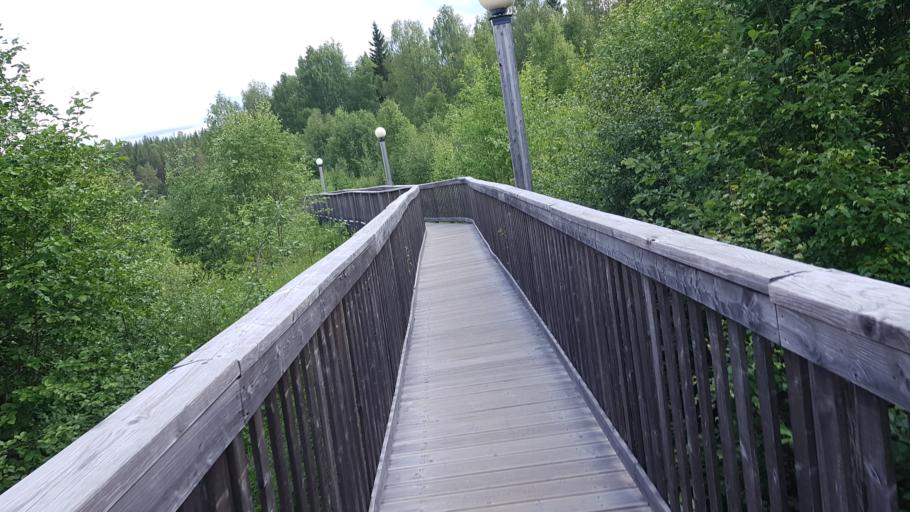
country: SE
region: Norrbotten
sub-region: Alvsbyns Kommun
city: AElvsbyn
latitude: 65.8554
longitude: 20.4158
